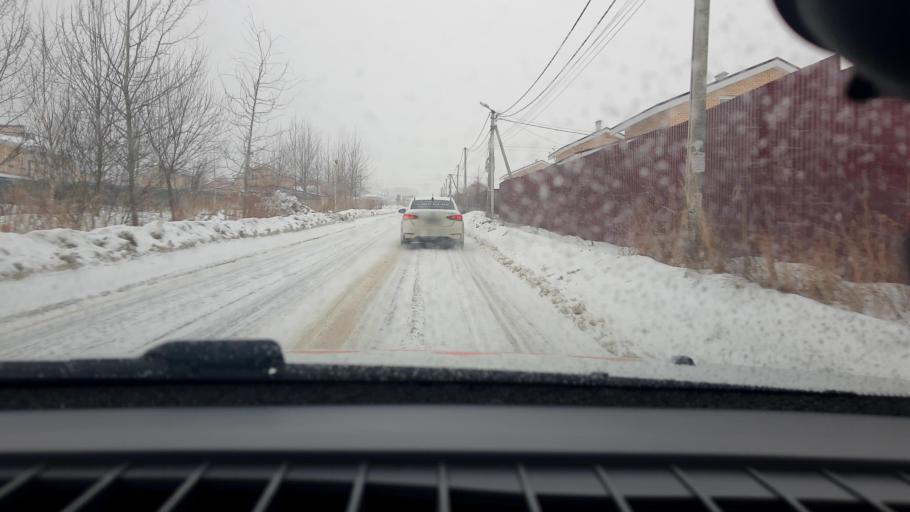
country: RU
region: Nizjnij Novgorod
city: Afonino
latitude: 56.1972
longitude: 44.0953
